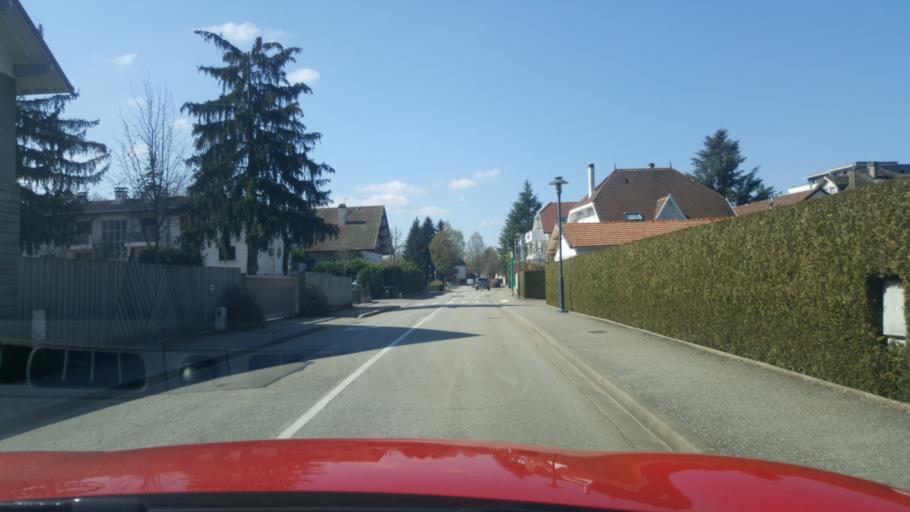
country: FR
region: Rhone-Alpes
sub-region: Departement de la Haute-Savoie
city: Annecy-le-Vieux
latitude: 45.9071
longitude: 6.1501
